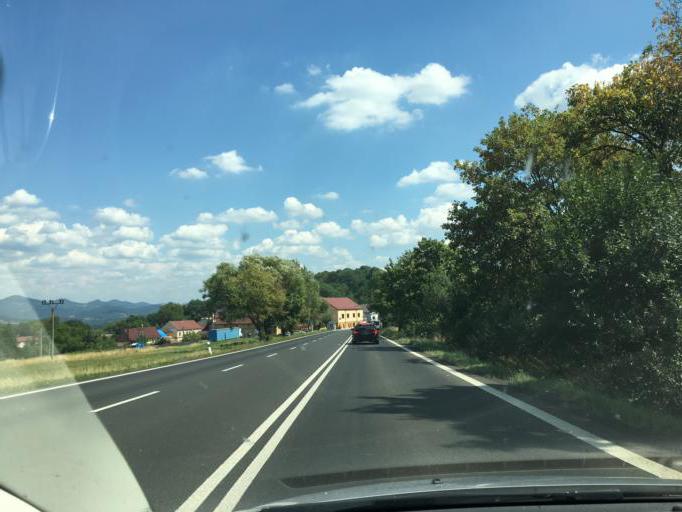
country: CZ
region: Ustecky
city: Benesov nad Ploucnici
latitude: 50.7896
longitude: 14.2996
